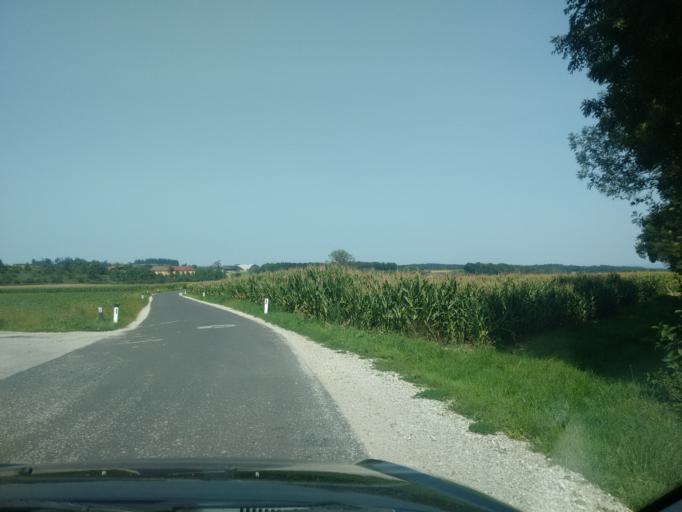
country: AT
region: Upper Austria
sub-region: Wels-Land
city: Gunskirchen
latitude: 48.1633
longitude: 13.9660
